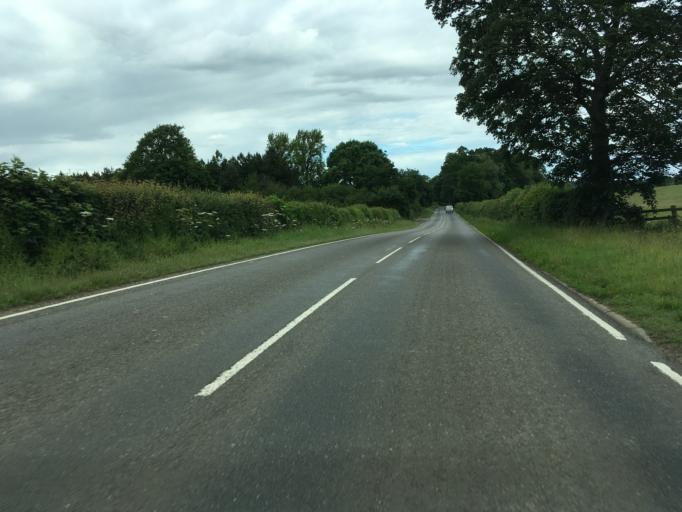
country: GB
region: England
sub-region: Central Bedfordshire
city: Potsgrove
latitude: 51.9690
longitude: -0.6432
